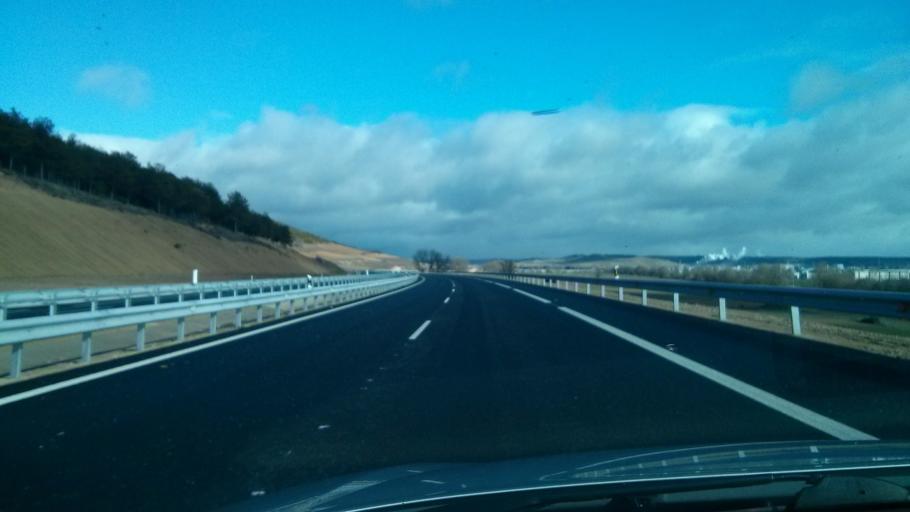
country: ES
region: Castille and Leon
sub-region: Provincia de Burgos
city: Villalbilla de Burgos
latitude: 42.3673
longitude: -3.7688
